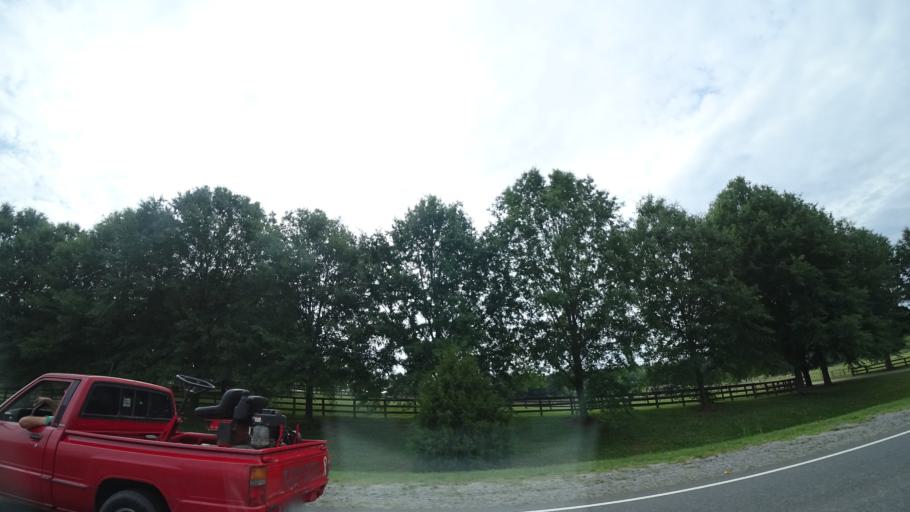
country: US
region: Virginia
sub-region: Spotsylvania County
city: Spotsylvania
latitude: 38.2200
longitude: -77.5685
